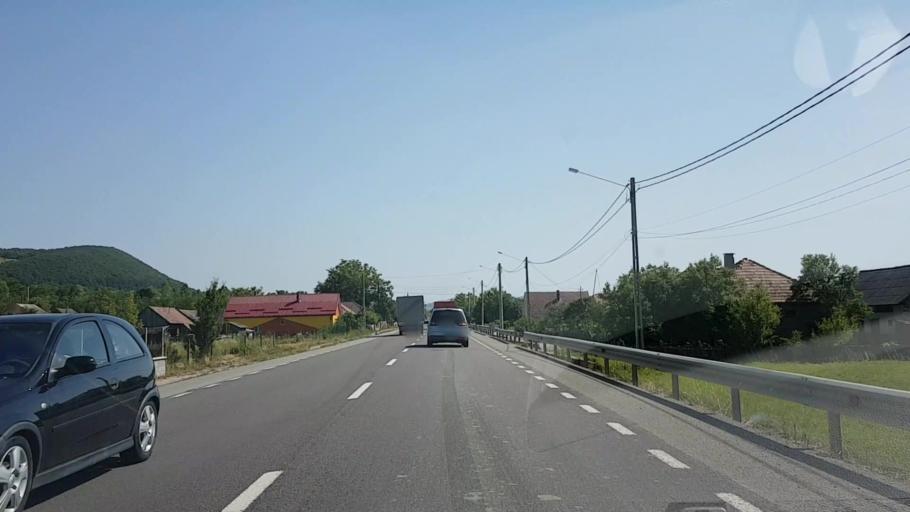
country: RO
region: Bistrita-Nasaud
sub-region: Comuna Sieu-Odorhei
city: Sieu-Odorhei
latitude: 47.1539
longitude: 24.3060
